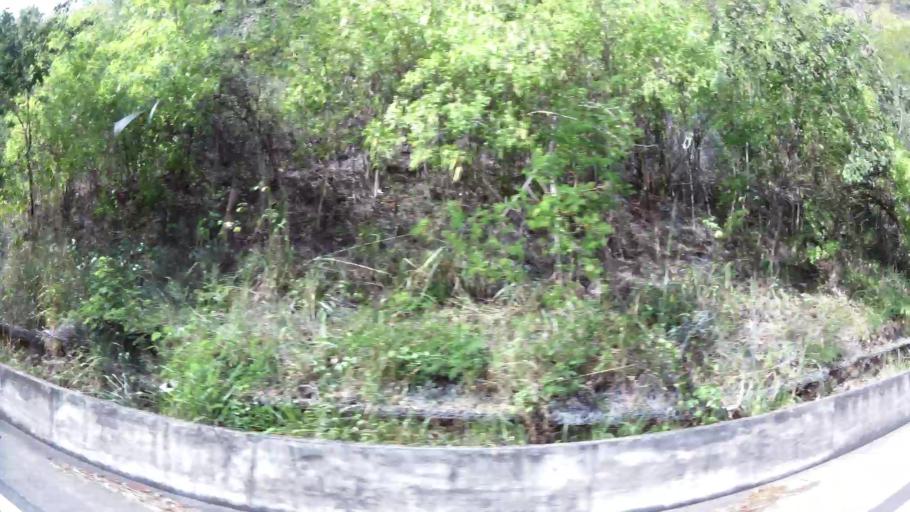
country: GP
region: Guadeloupe
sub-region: Guadeloupe
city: Baillif
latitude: 16.0374
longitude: -61.7486
